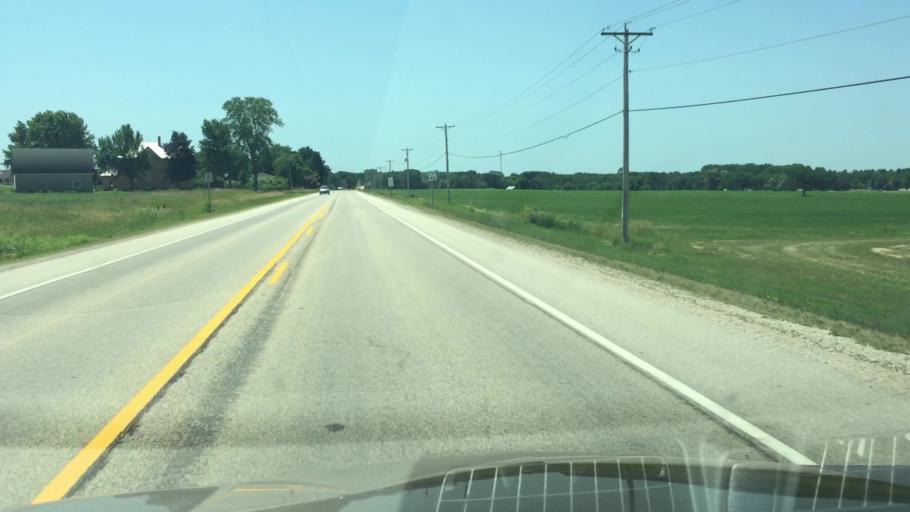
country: US
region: Wisconsin
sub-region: Fond du Lac County
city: Saint Peter
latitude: 43.9256
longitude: -88.3066
